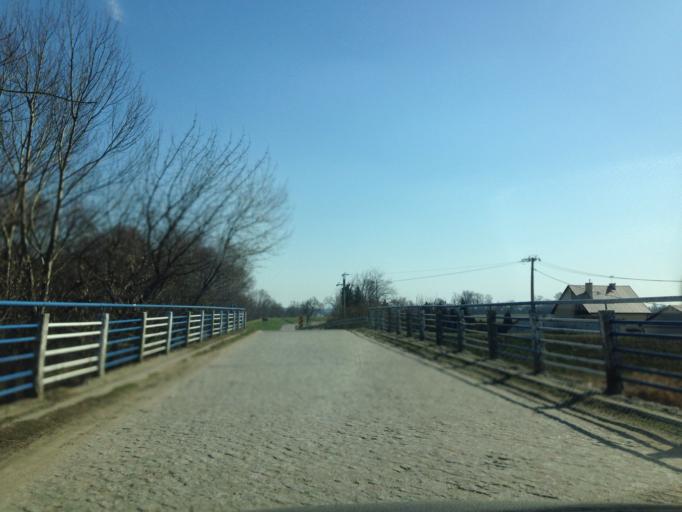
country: PL
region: Masovian Voivodeship
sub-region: Powiat piaseczynski
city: Konstancin-Jeziorna
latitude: 52.1208
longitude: 21.1743
